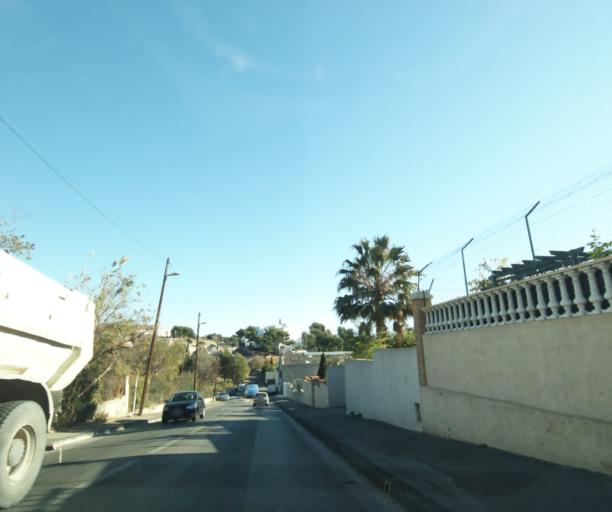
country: FR
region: Provence-Alpes-Cote d'Azur
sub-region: Departement des Bouches-du-Rhone
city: Marseille 14
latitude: 43.3576
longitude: 5.3662
